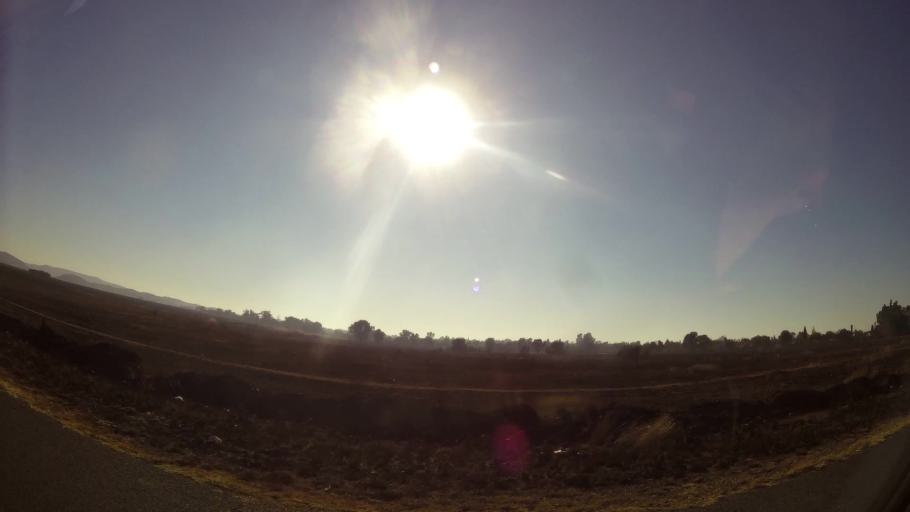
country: ZA
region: Gauteng
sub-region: City of Johannesburg Metropolitan Municipality
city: Johannesburg
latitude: -26.3325
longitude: 28.0775
